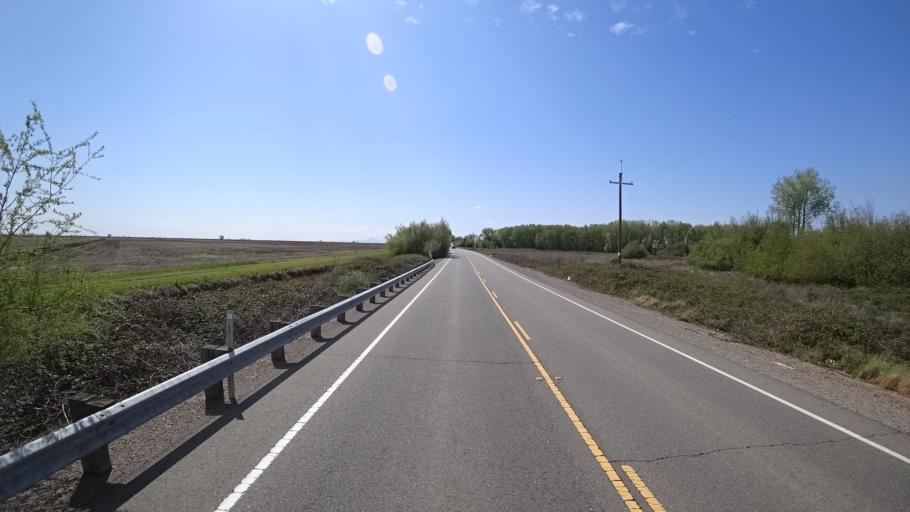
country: US
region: California
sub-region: Butte County
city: Durham
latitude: 39.5296
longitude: -121.8565
